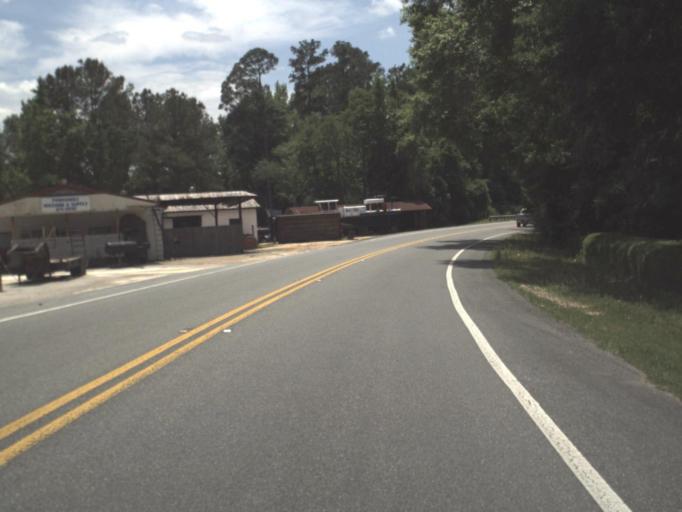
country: US
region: Florida
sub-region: Calhoun County
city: Blountstown
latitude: 30.4388
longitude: -85.0461
